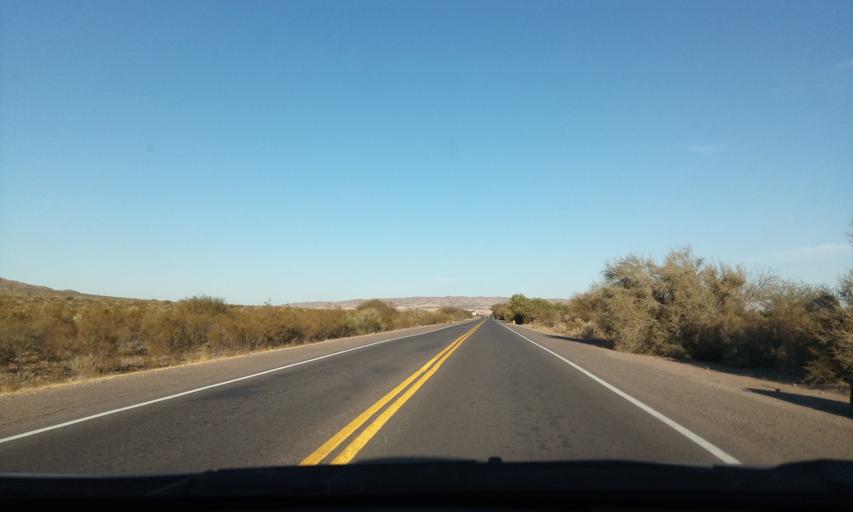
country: AR
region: San Juan
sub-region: Departamento de Rivadavia
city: Rivadavia
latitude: -31.4288
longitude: -68.6685
